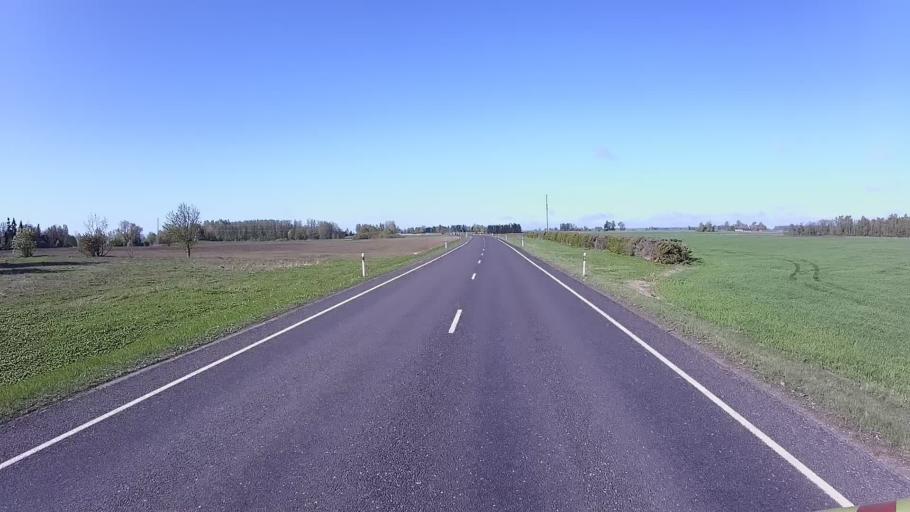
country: EE
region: Viljandimaa
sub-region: Vohma linn
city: Vohma
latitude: 58.6818
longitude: 25.6113
